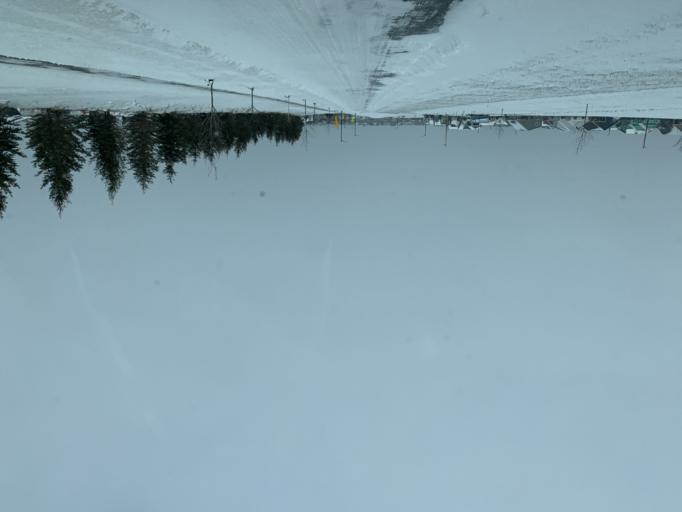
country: US
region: Minnesota
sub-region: Washington County
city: Cottage Grove
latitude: 44.8742
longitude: -92.9235
